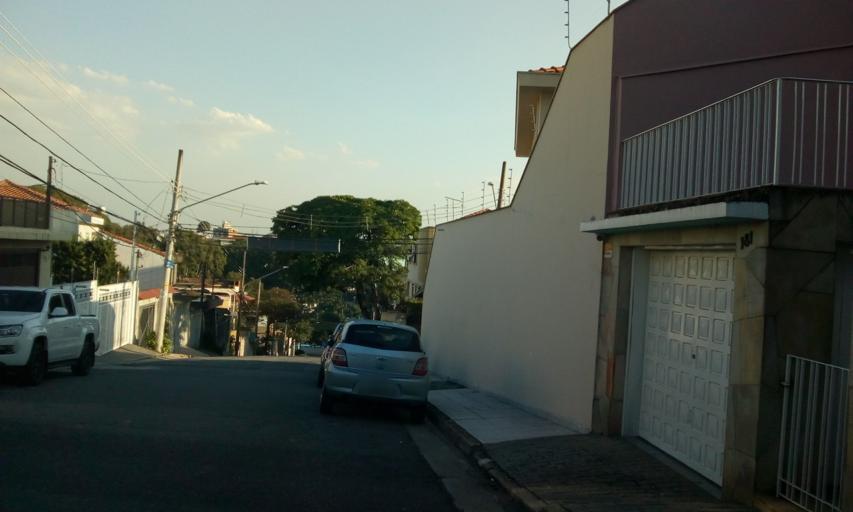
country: BR
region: Sao Paulo
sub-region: Sao Paulo
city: Sao Paulo
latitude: -23.4926
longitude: -46.6133
